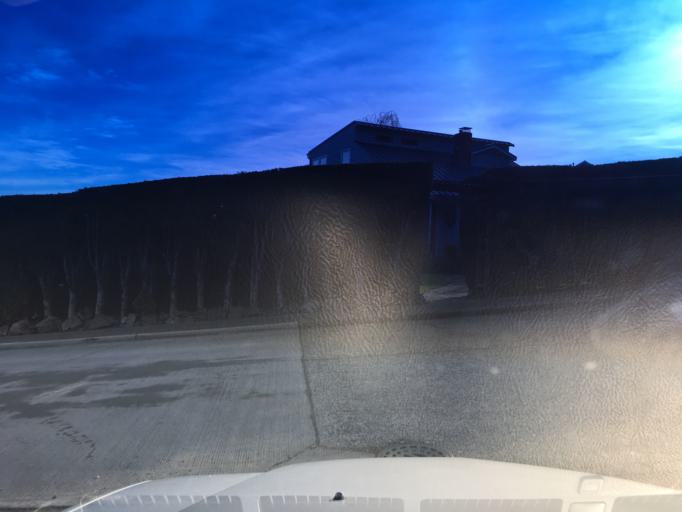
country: US
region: Washington
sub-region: King County
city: Inglewood-Finn Hill
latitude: 47.6830
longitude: -122.2668
